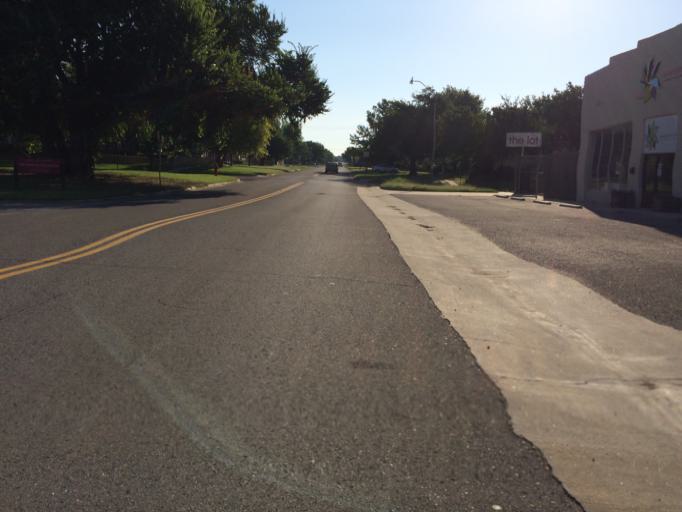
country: US
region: Oklahoma
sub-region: Cleveland County
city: Norman
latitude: 35.2230
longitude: -97.4383
